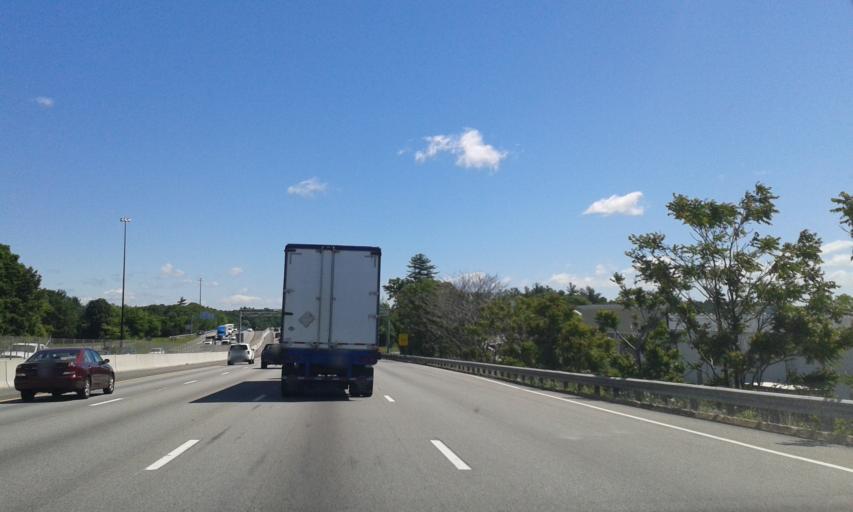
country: US
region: Massachusetts
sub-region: Middlesex County
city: Burlington
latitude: 42.4855
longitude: -71.1953
